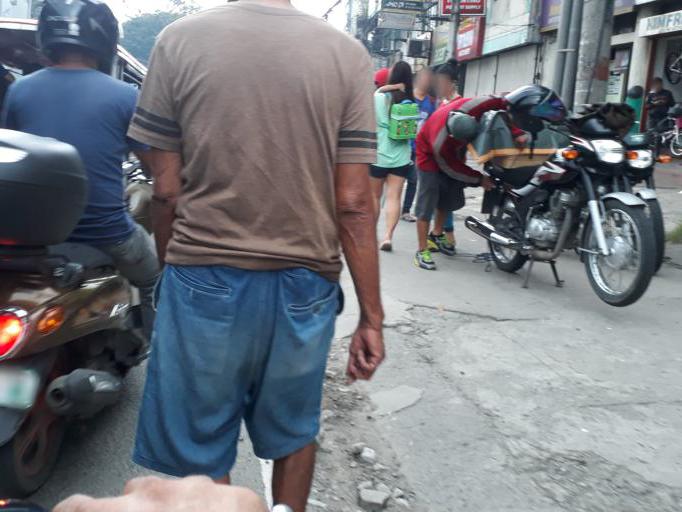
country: PH
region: Calabarzon
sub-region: Province of Rizal
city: Valenzuela
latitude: 14.6913
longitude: 120.9728
